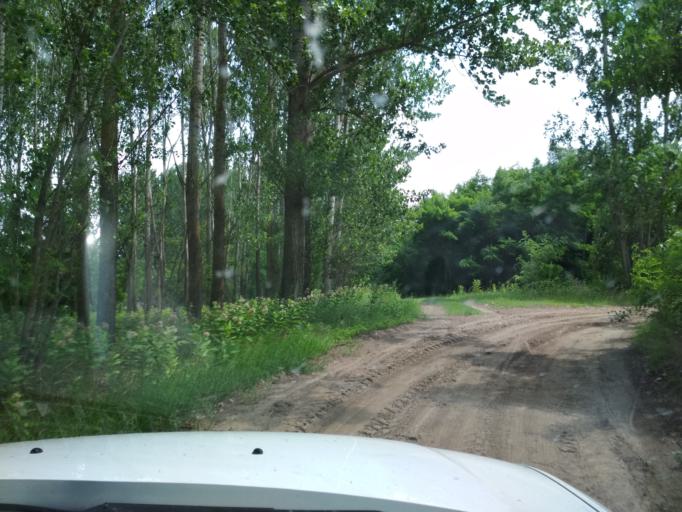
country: HU
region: Pest
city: Tapioszentmarton
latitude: 47.3582
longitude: 19.7468
